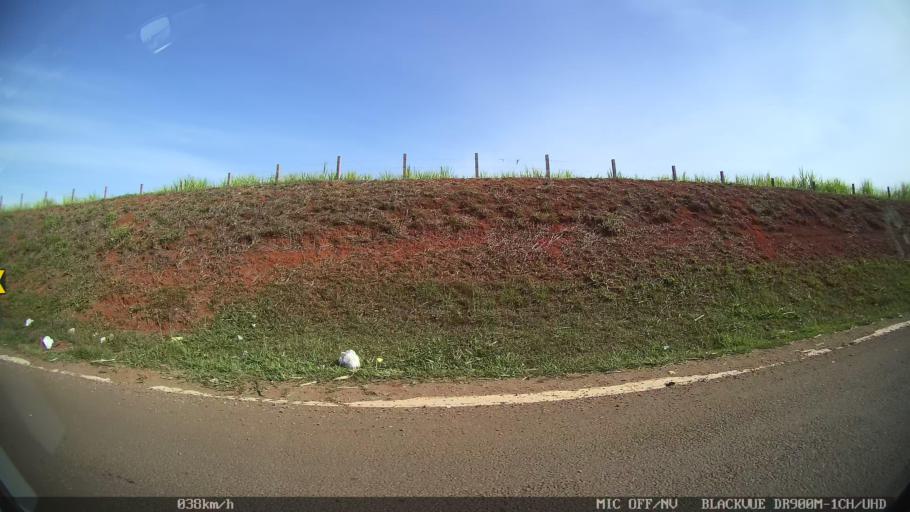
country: BR
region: Sao Paulo
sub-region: Piracicaba
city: Piracicaba
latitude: -22.7808
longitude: -47.6534
